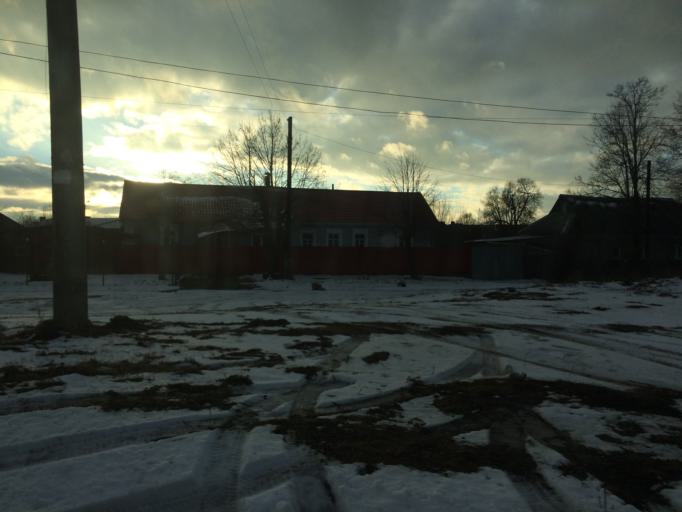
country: RU
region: Tula
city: Cherepet'
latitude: 54.1082
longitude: 36.3286
